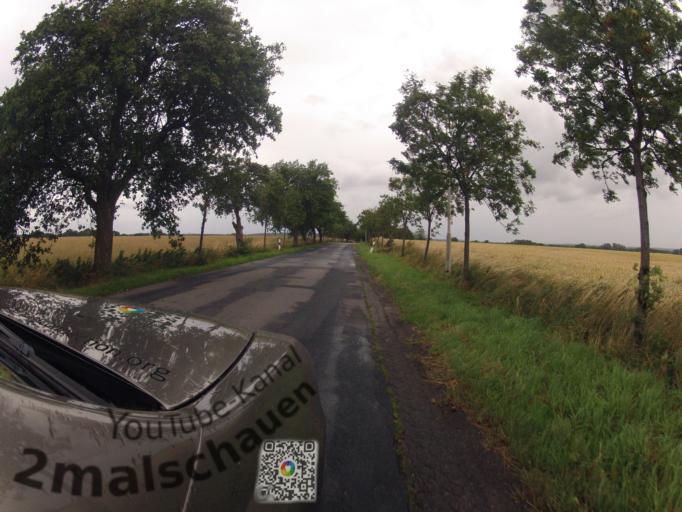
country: DE
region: Mecklenburg-Vorpommern
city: Seebad Bansin
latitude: 53.8915
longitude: 14.0724
